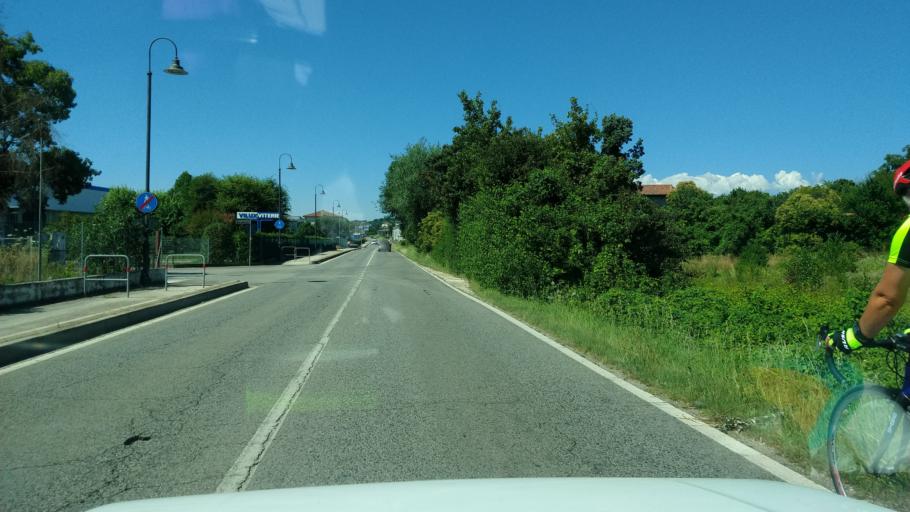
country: IT
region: Veneto
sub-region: Provincia di Vicenza
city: Pianezze
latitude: 45.7282
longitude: 11.6237
